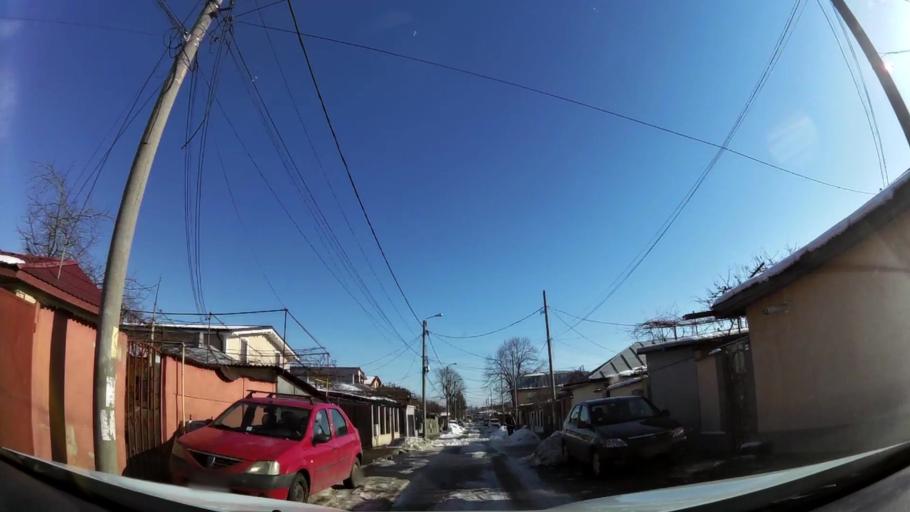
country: RO
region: Ilfov
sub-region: Comuna Magurele
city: Magurele
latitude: 44.3972
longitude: 26.0527
